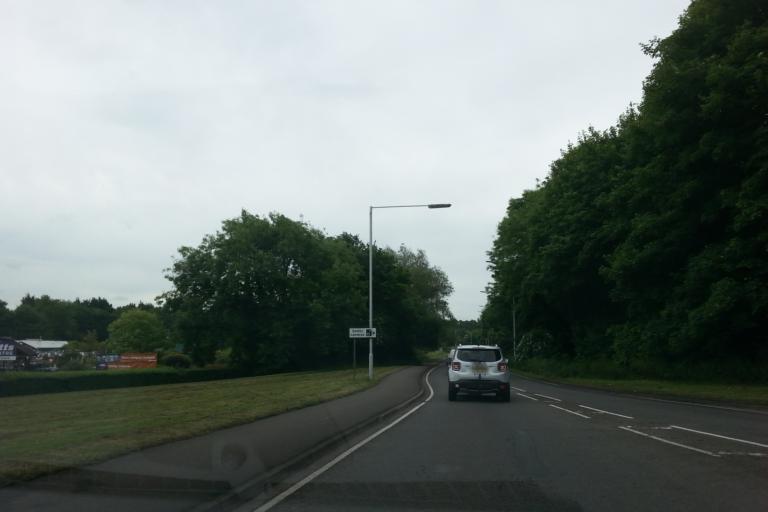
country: GB
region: England
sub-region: Peterborough
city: Marholm
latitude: 52.5559
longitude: -0.2988
